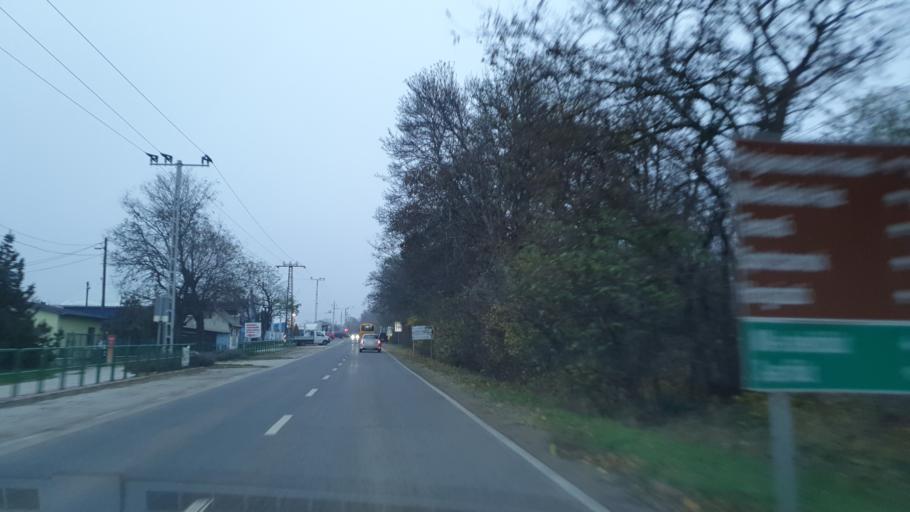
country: HU
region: Pest
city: Csomor
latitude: 47.5436
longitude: 19.2167
